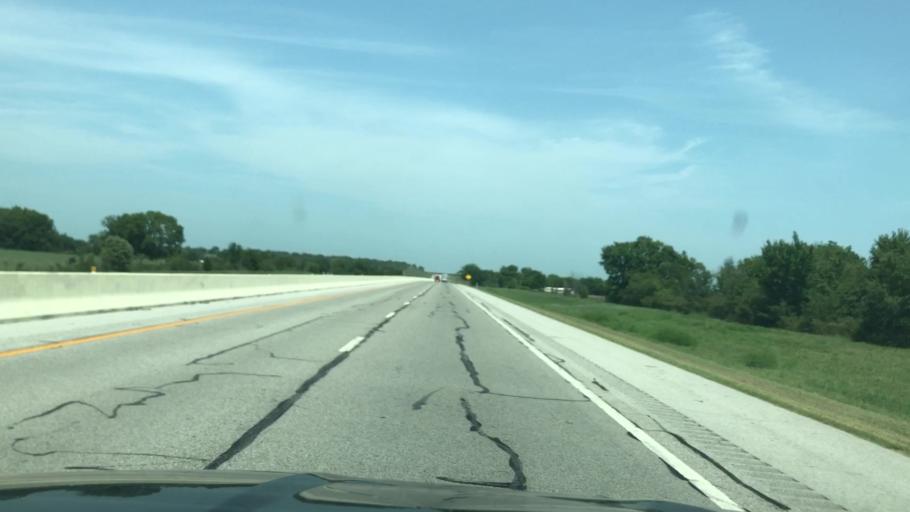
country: US
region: Oklahoma
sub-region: Rogers County
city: Chelsea
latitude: 36.4778
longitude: -95.3207
